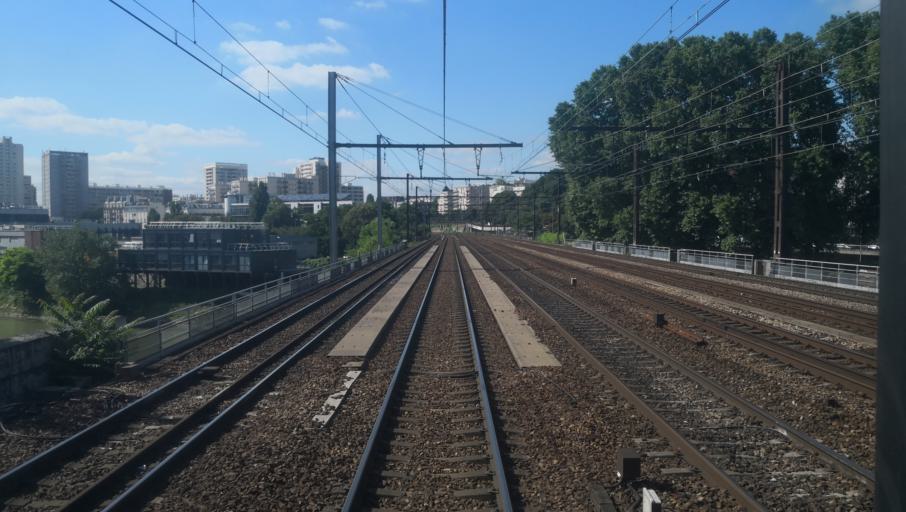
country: FR
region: Ile-de-France
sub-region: Departement du Val-de-Marne
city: Charenton-le-Pont
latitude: 48.8158
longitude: 2.4163
